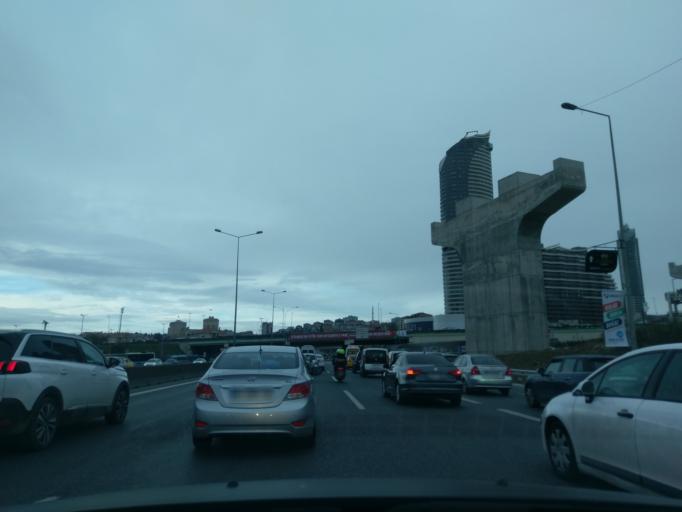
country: TR
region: Istanbul
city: UEskuedar
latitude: 40.9980
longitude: 29.0588
